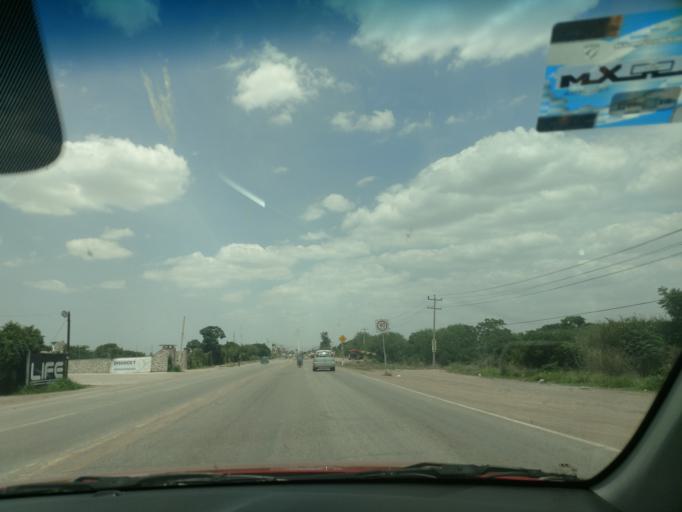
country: MX
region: San Luis Potosi
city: Ciudad Fernandez
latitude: 21.9391
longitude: -100.0350
